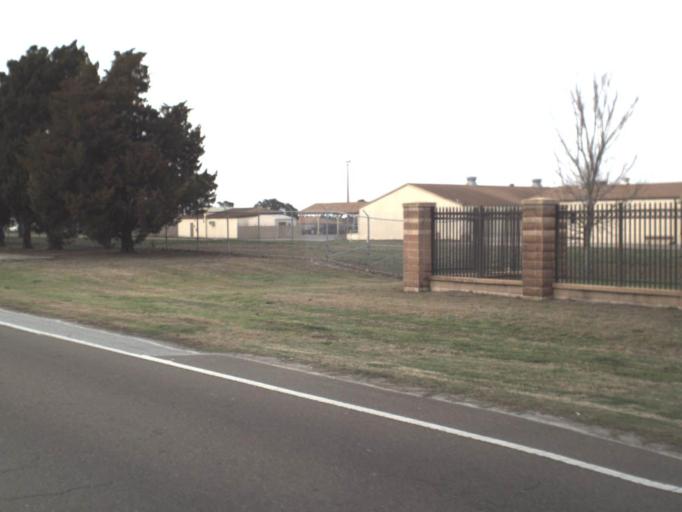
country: US
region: Florida
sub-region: Bay County
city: Tyndall Air Force Base
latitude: 30.0711
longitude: -85.5915
